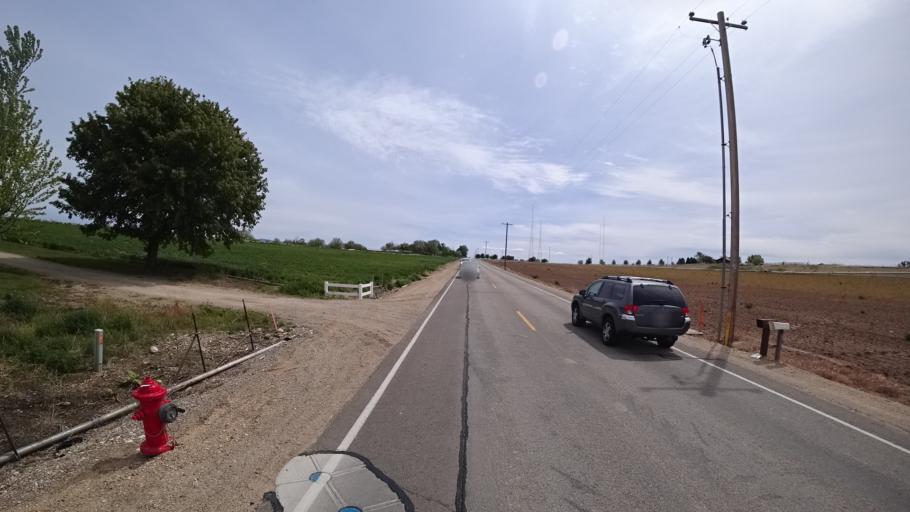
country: US
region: Idaho
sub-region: Ada County
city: Meridian
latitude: 43.5611
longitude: -116.4078
